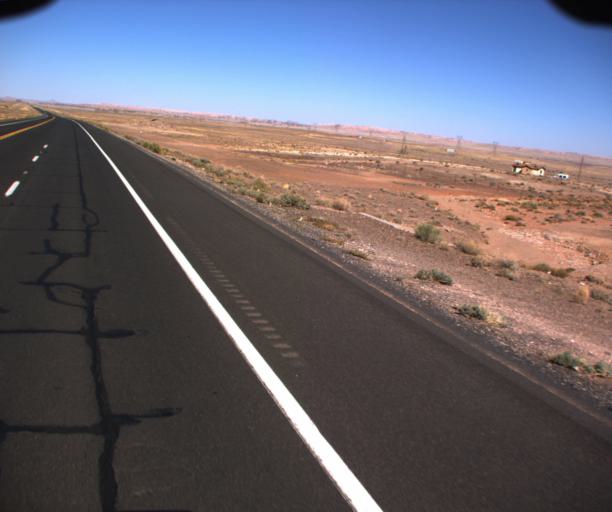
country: US
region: Arizona
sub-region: Coconino County
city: Tuba City
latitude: 35.8939
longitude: -111.4065
